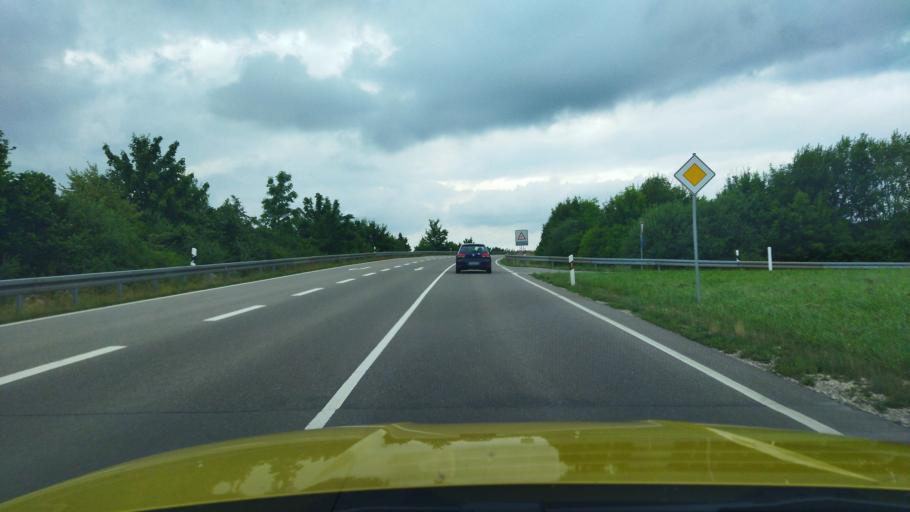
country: DE
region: Bavaria
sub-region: Regierungsbezirk Mittelfranken
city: Muhr am See
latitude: 49.1439
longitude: 10.7351
